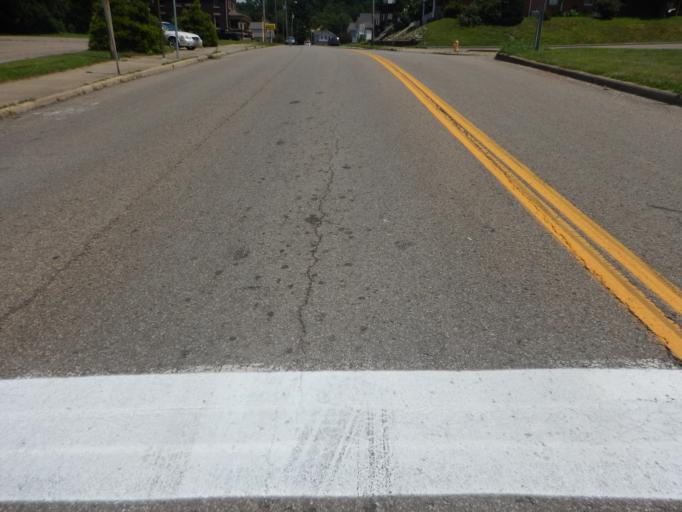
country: US
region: Ohio
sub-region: Muskingum County
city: Zanesville
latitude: 39.9409
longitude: -82.0013
